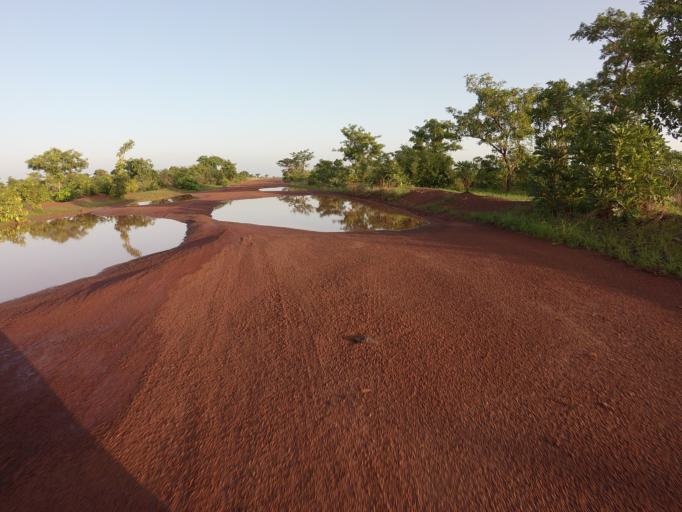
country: TG
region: Savanes
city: Sansanne-Mango
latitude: 10.2346
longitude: -0.0738
